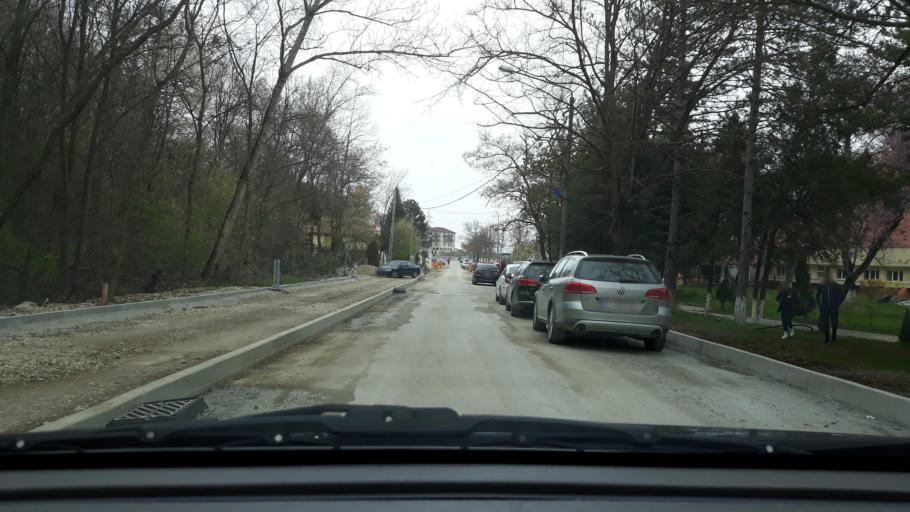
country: RO
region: Bihor
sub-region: Comuna Sanmartin
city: Sanmartin
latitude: 46.9943
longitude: 21.9779
